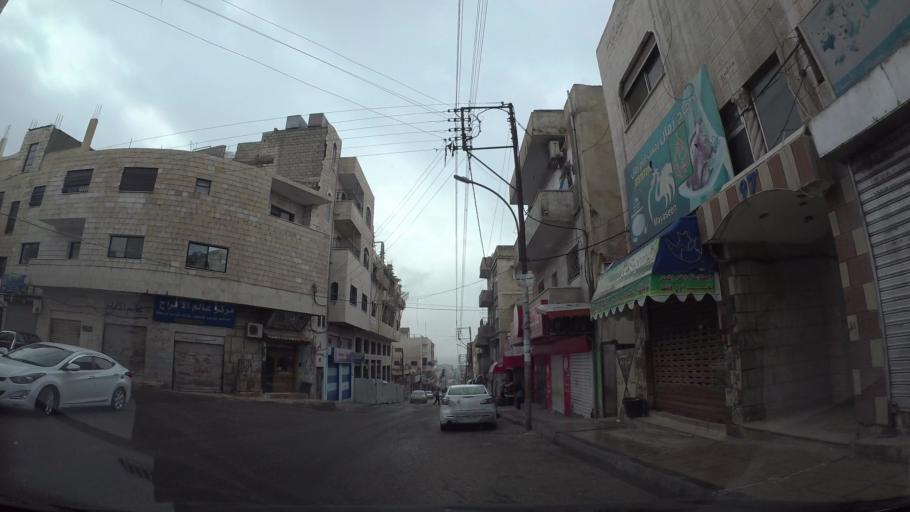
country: JO
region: Amman
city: Amman
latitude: 31.9680
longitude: 35.9285
